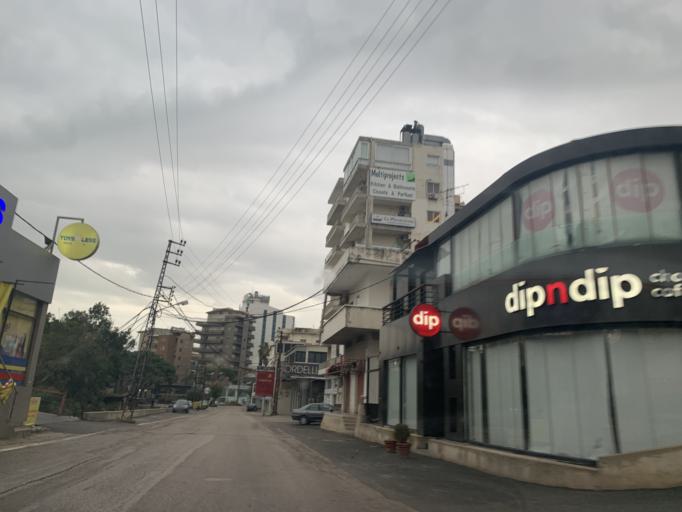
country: LB
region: Mont-Liban
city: Djounie
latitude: 33.9811
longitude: 35.6164
